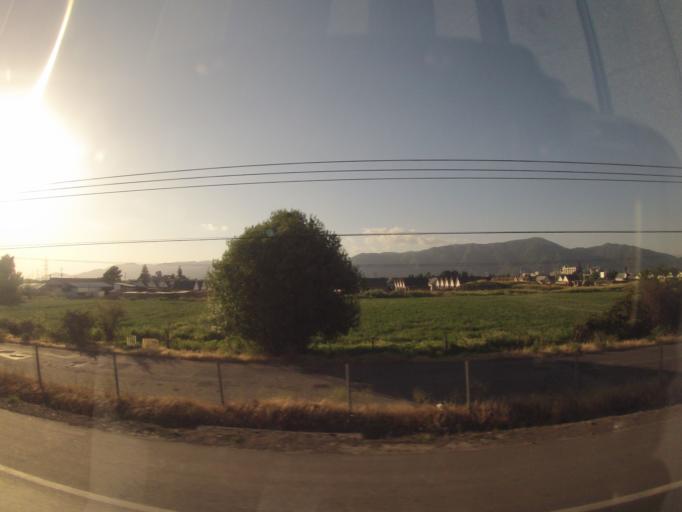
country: CL
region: O'Higgins
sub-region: Provincia de Colchagua
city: Chimbarongo
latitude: -34.6002
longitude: -70.9780
